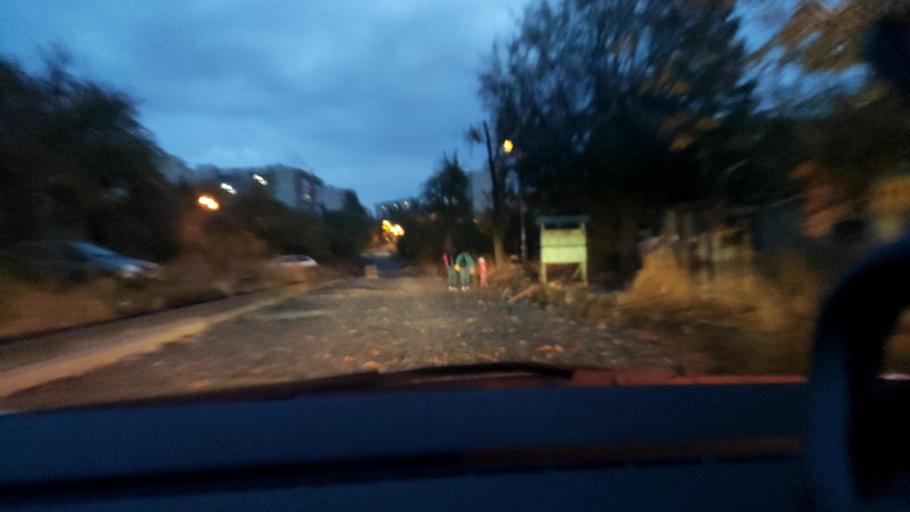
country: RU
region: Voronezj
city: Voronezh
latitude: 51.6921
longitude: 39.1972
